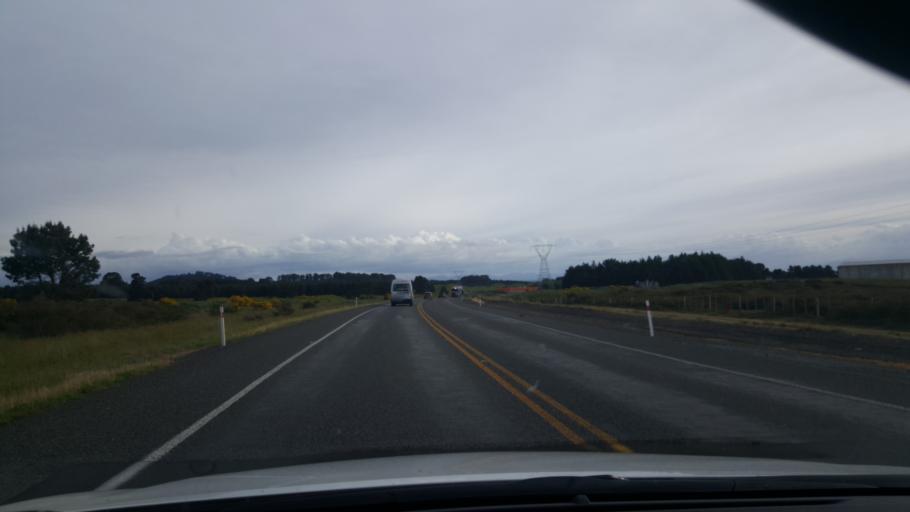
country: NZ
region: Waikato
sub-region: Taupo District
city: Taupo
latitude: -38.6933
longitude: 176.1138
